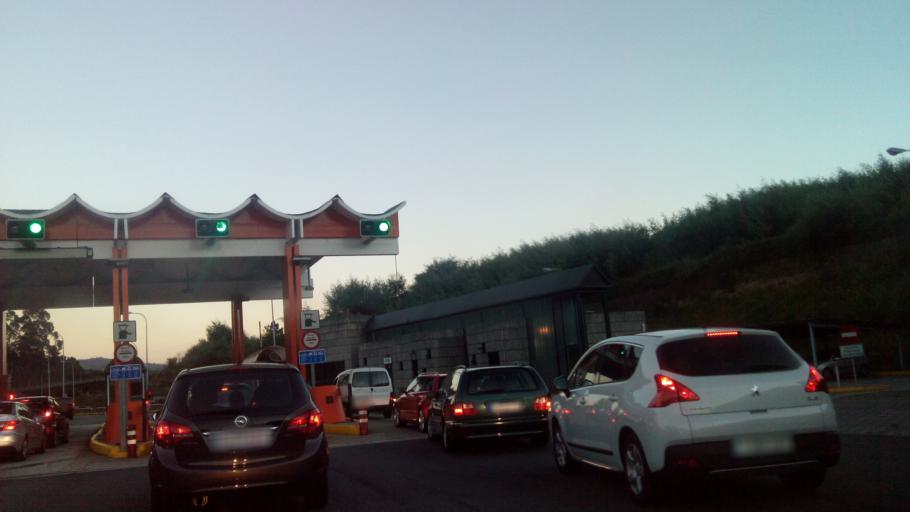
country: ES
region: Galicia
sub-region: Provincia de Pontevedra
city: Pontevedra
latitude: 42.4466
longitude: -8.6494
